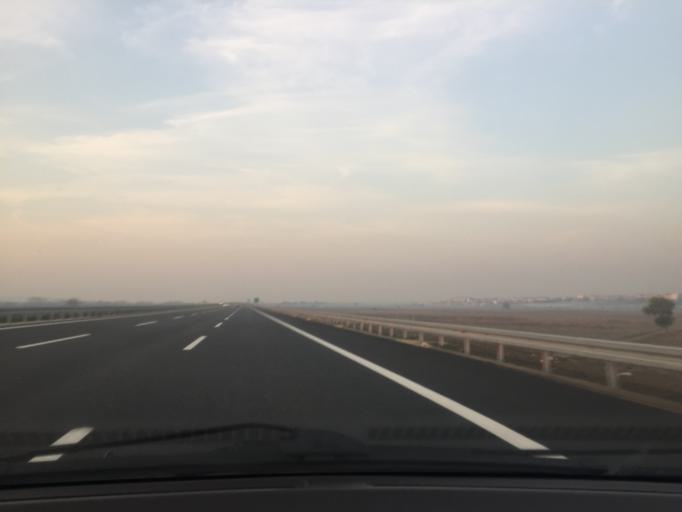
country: TR
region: Bursa
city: Karacabey
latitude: 40.2131
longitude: 28.3900
